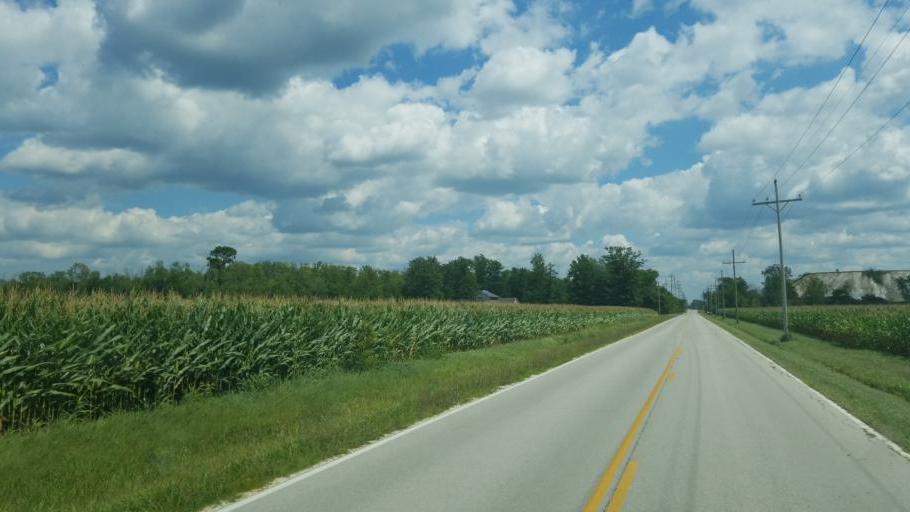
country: US
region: Ohio
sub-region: Sandusky County
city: Gibsonburg
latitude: 41.3990
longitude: -83.3380
